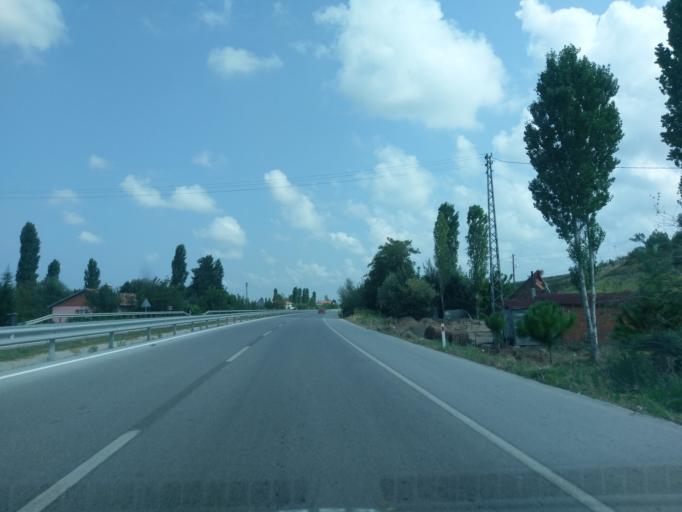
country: TR
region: Samsun
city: Alacam
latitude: 41.6118
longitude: 35.7048
